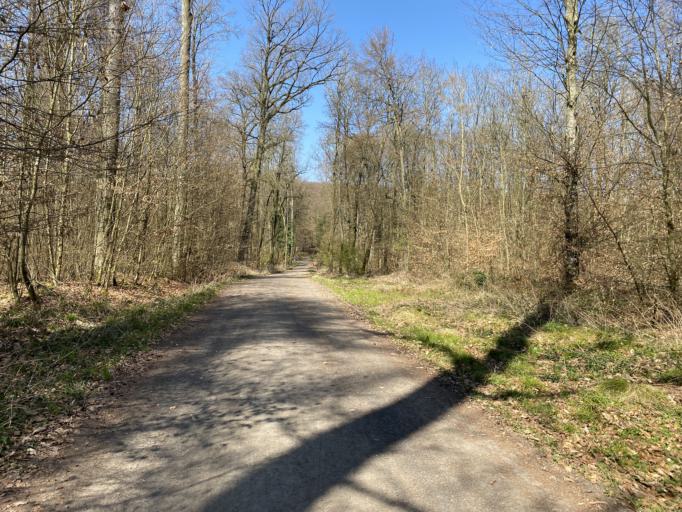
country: DE
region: Hesse
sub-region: Regierungsbezirk Darmstadt
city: Langenselbold
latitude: 50.2307
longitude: 9.0742
